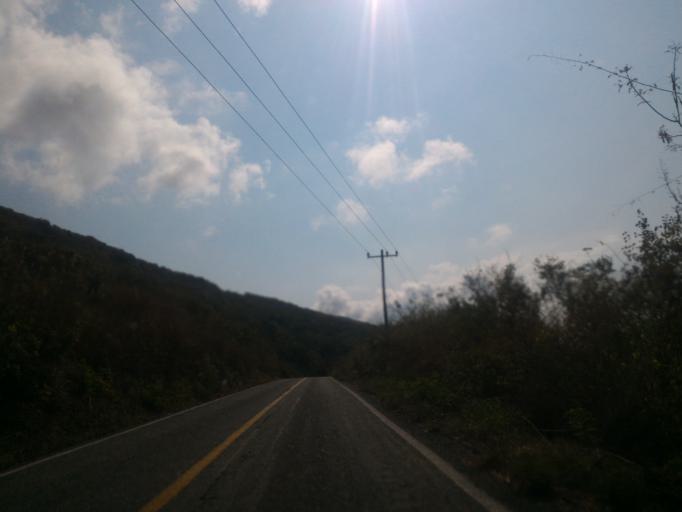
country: MX
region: Michoacan
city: Coahuayana Viejo
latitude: 18.4856
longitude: -103.5699
